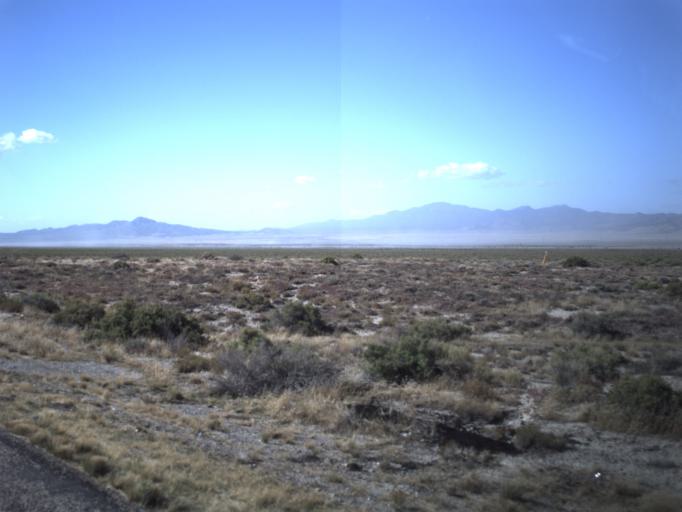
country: US
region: Utah
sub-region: Beaver County
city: Milford
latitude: 38.6847
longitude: -112.9770
